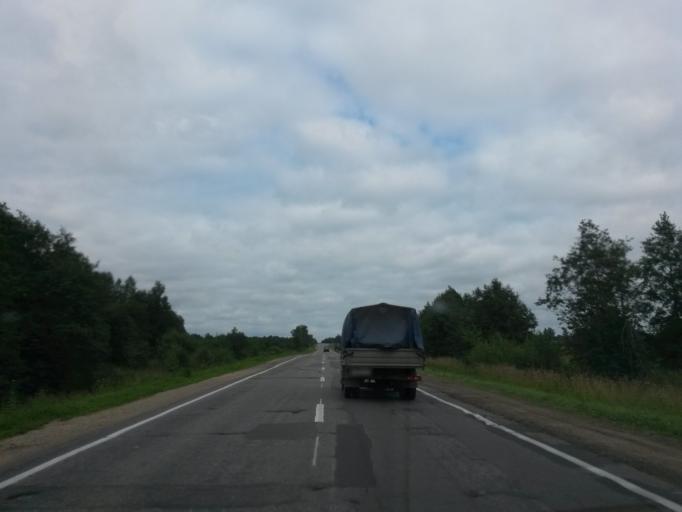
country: RU
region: Jaroslavl
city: Gavrilov-Yam
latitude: 57.4407
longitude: 39.9171
